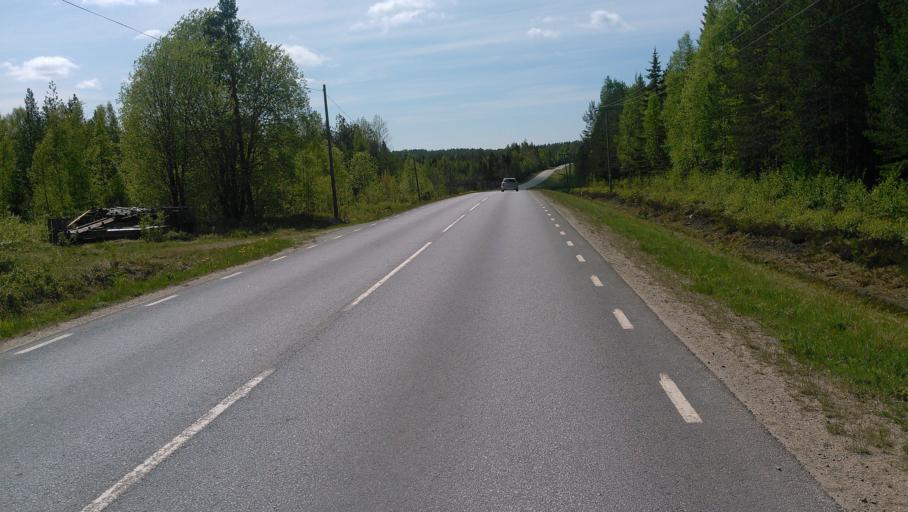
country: SE
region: Vaesterbotten
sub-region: Vannas Kommun
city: Vannasby
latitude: 63.8581
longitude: 20.0019
